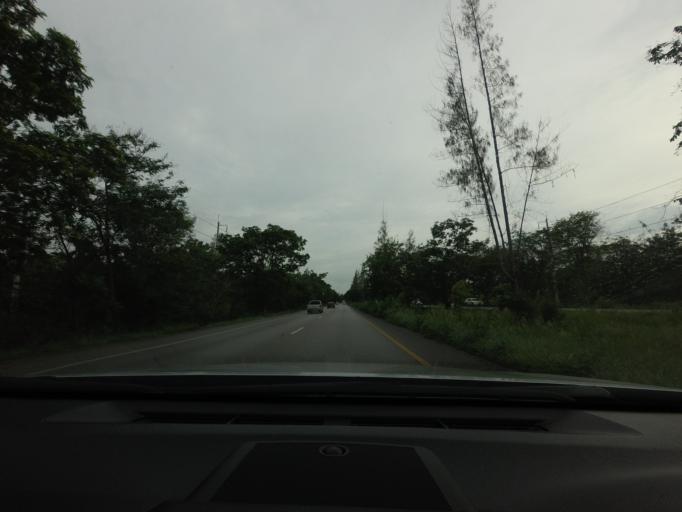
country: TH
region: Phetchaburi
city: Cha-am
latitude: 12.6929
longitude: 99.9025
